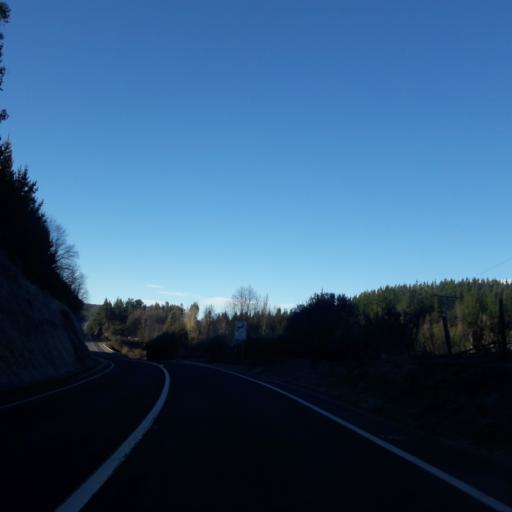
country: CL
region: Biobio
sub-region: Provincia de Biobio
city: La Laja
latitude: -37.2802
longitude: -72.9467
